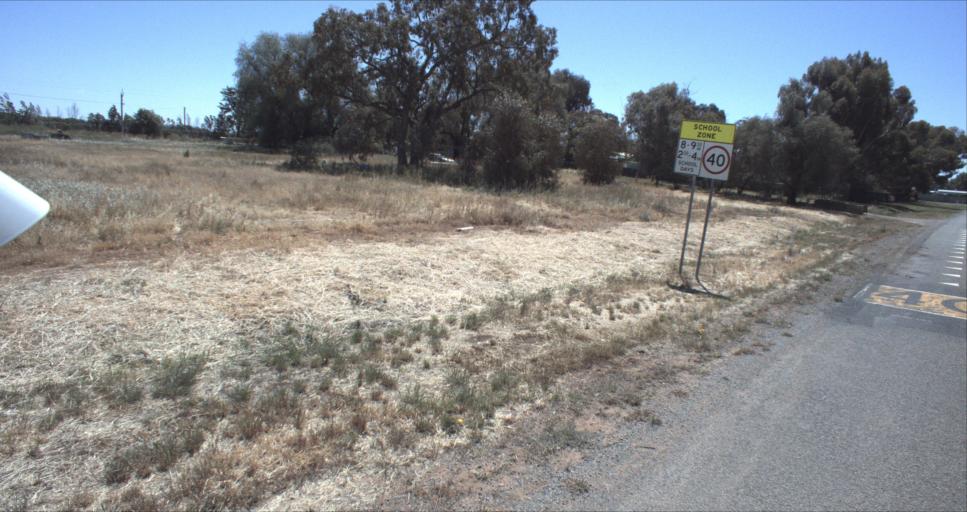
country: AU
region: New South Wales
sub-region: Leeton
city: Leeton
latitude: -34.5269
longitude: 146.3313
